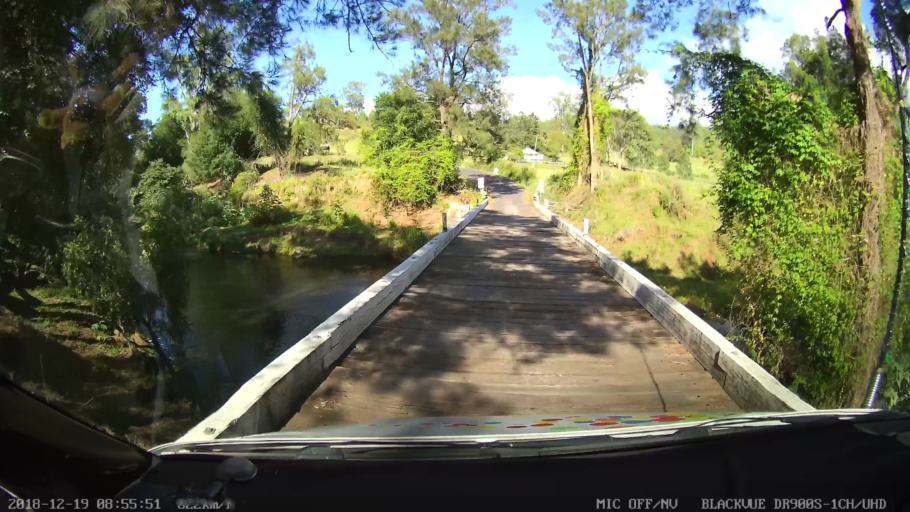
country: AU
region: New South Wales
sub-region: Kyogle
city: Kyogle
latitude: -28.4169
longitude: 152.9772
